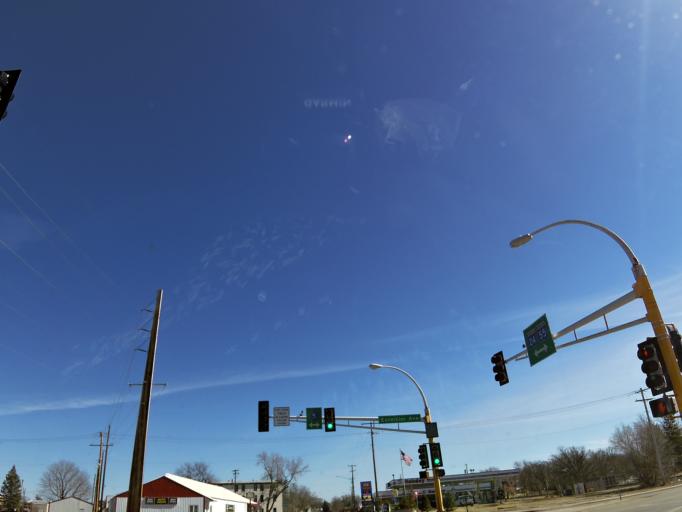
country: US
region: Minnesota
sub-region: Wright County
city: Annandale
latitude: 45.2627
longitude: -94.1276
